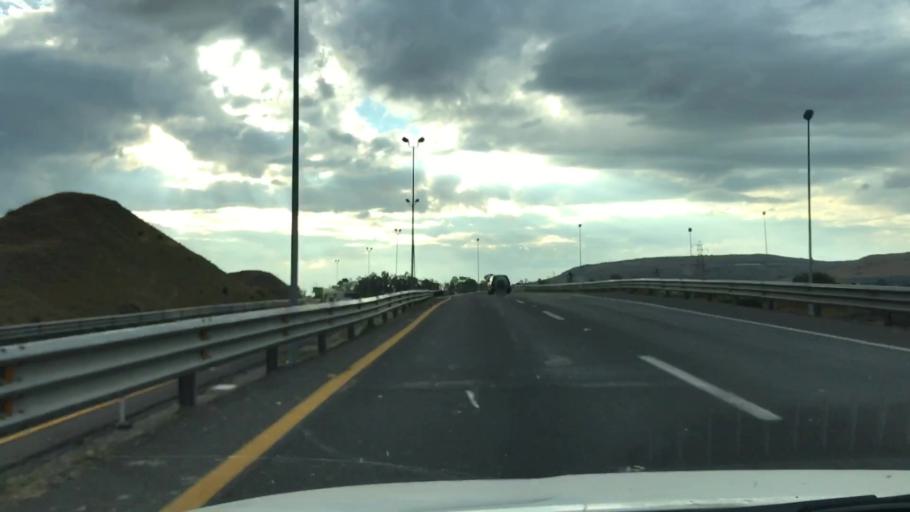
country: MX
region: Guanajuato
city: Penjamo
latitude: 20.4193
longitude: -101.7235
